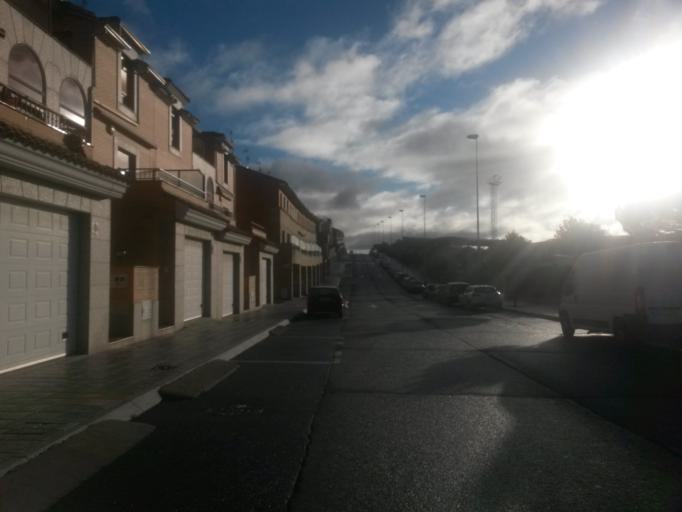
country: ES
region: Castille and Leon
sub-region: Provincia de Salamanca
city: Salamanca
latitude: 40.9792
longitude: -5.6489
